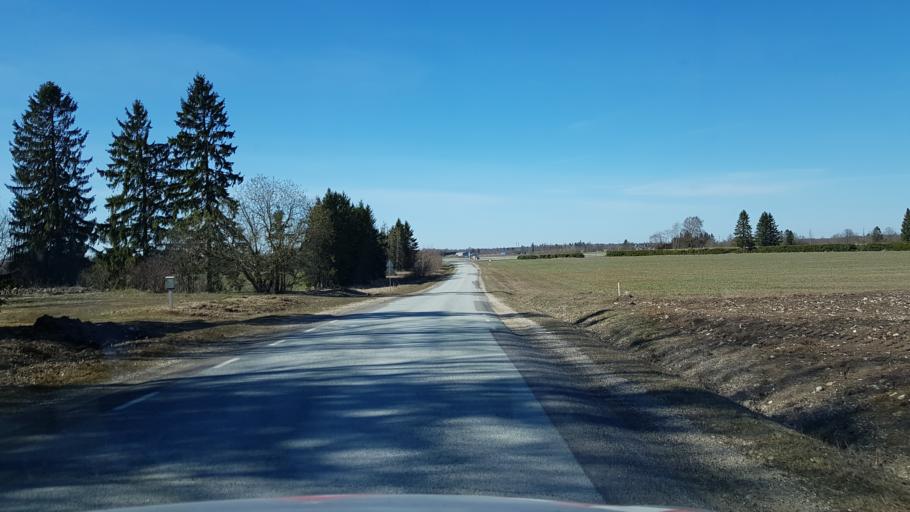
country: EE
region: Laeaene-Virumaa
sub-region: Someru vald
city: Someru
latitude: 59.3632
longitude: 26.4649
